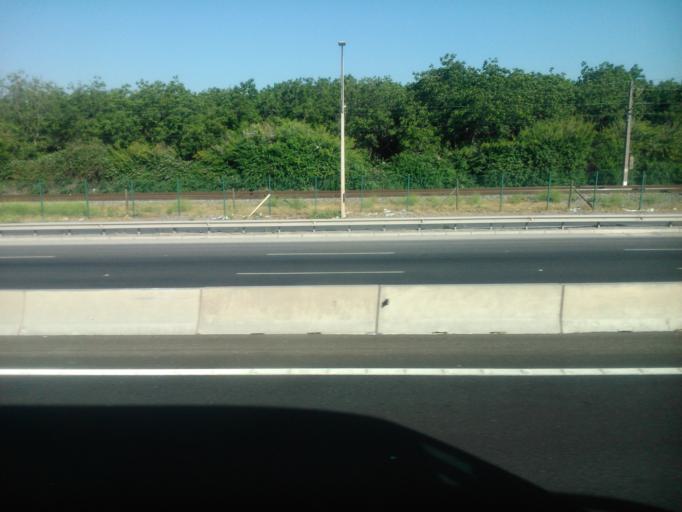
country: CL
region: Santiago Metropolitan
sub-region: Provincia de Maipo
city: San Bernardo
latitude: -33.6616
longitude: -70.7179
